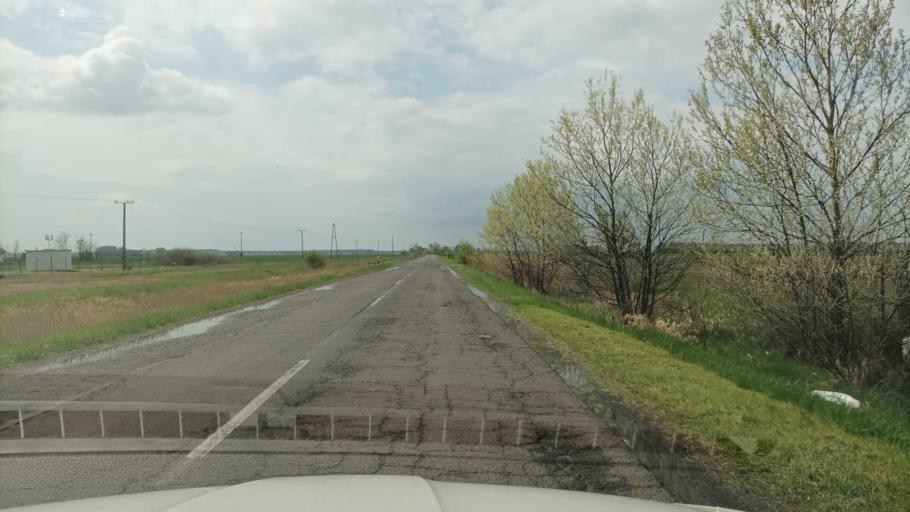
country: HU
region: Pest
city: Nagykoros
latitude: 47.0472
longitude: 19.8368
